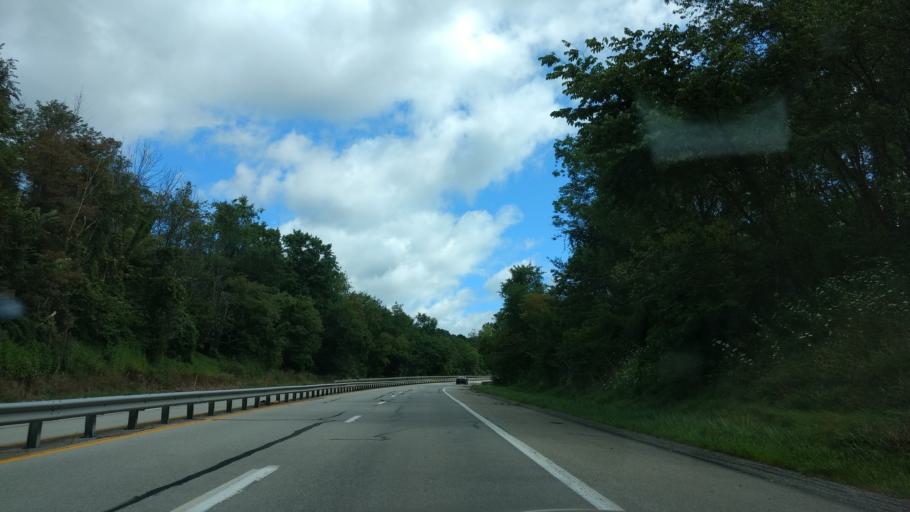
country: US
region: Pennsylvania
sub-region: Westmoreland County
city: Murrysville
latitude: 40.5154
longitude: -79.6443
